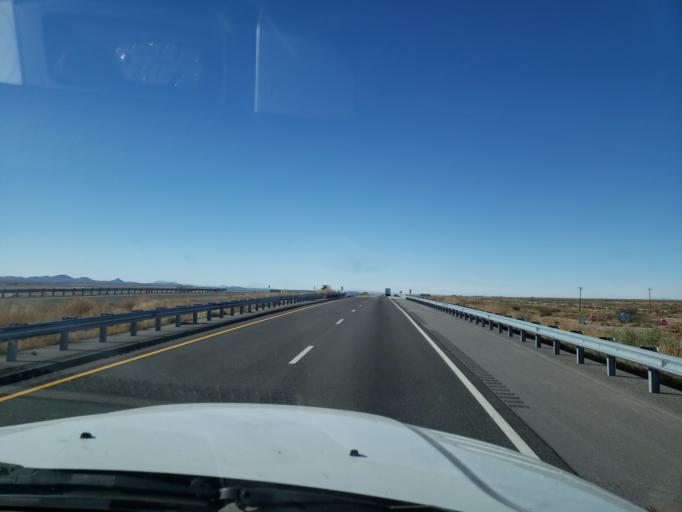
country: US
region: New Mexico
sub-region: Hidalgo County
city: Lordsburg
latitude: 32.3115
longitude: -108.6062
